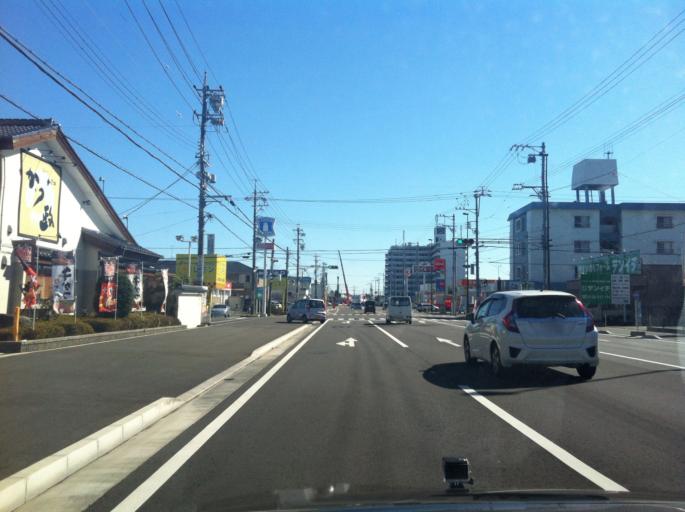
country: JP
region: Shizuoka
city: Shizuoka-shi
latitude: 34.9508
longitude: 138.4088
